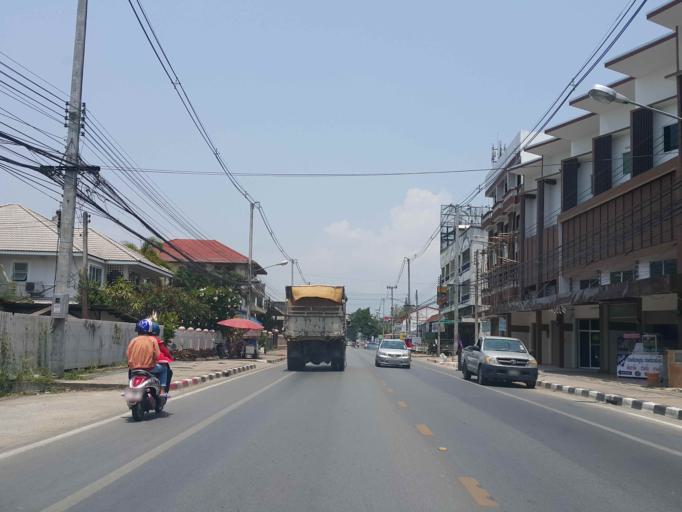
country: TH
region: Chiang Mai
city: Saraphi
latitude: 18.7776
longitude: 99.0541
